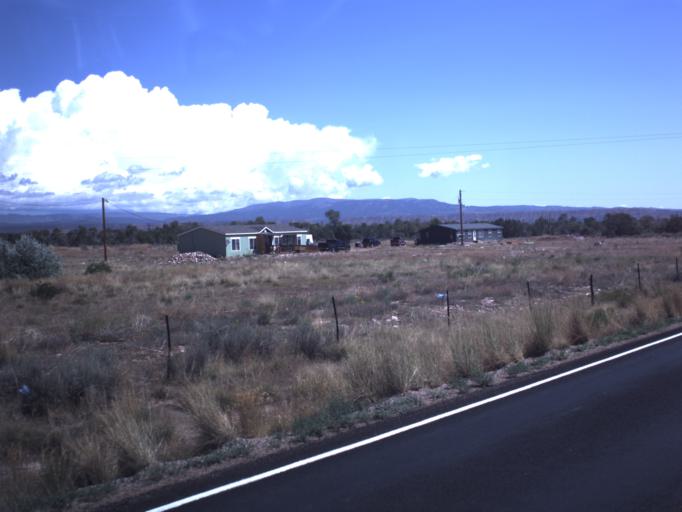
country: US
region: Utah
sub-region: Duchesne County
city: Roosevelt
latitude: 40.4038
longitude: -109.9016
